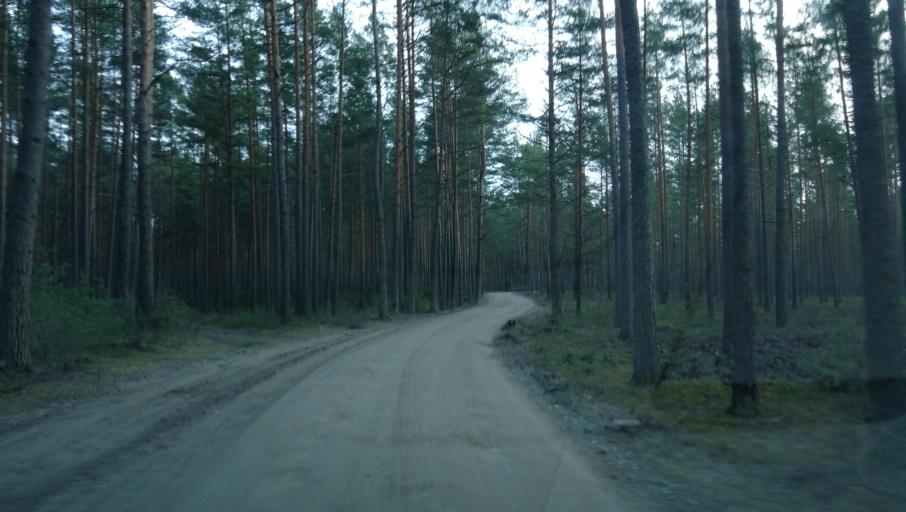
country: LV
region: Adazi
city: Adazi
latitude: 57.0573
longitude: 24.2964
